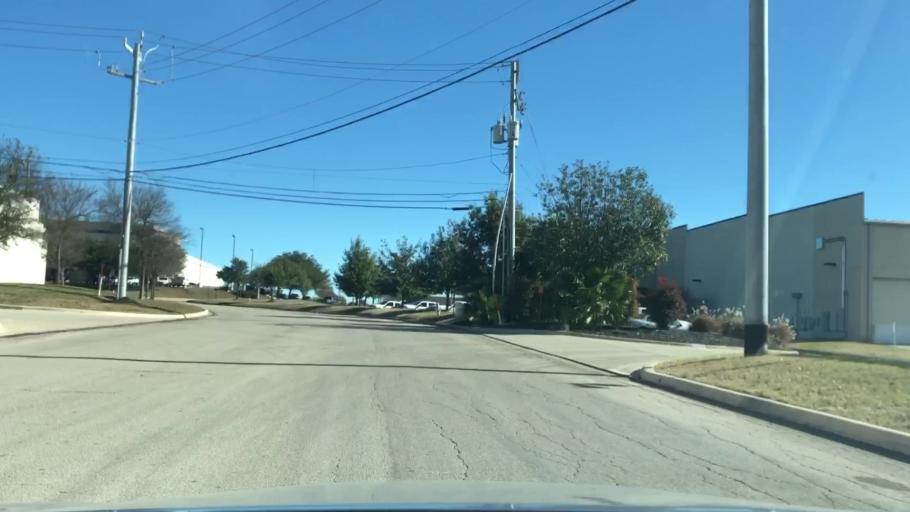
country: US
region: Texas
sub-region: Bexar County
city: Selma
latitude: 29.5996
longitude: -98.2827
